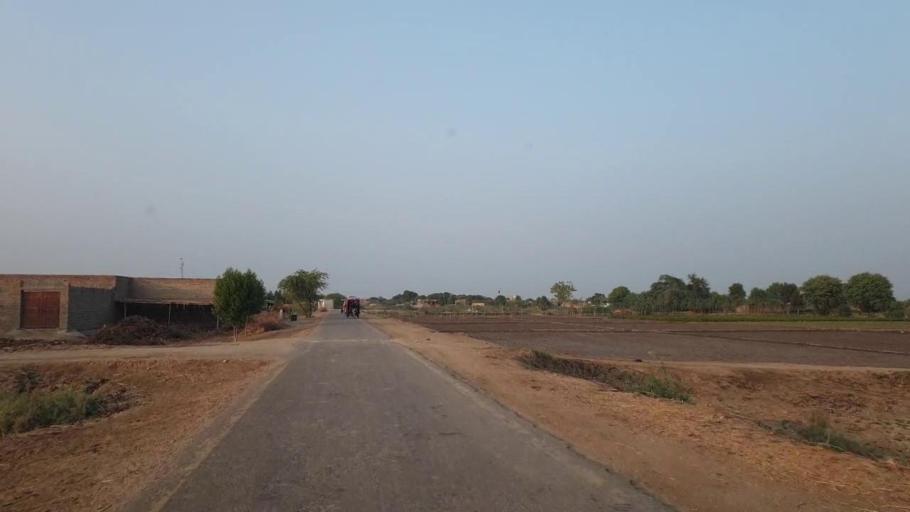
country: PK
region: Sindh
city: Tando Ghulam Ali
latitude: 25.1408
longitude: 68.9587
